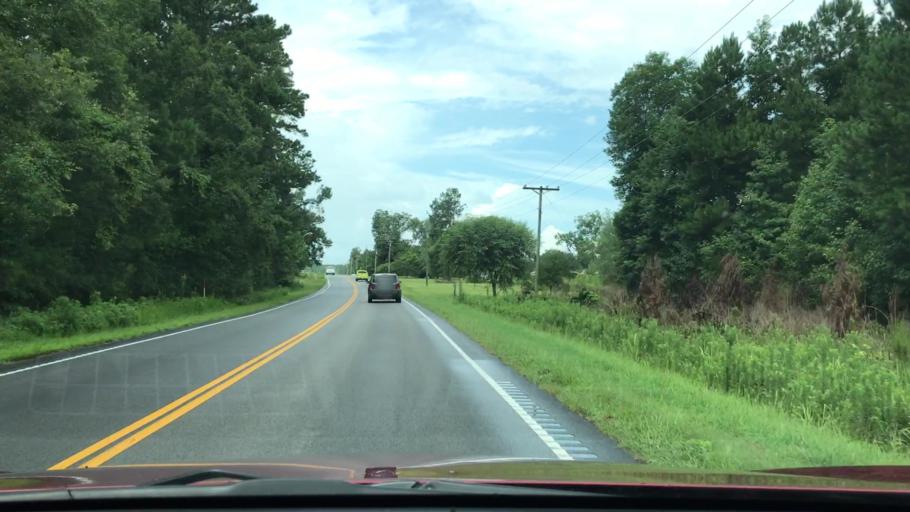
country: US
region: South Carolina
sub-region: Horry County
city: Loris
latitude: 33.9052
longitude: -78.8477
